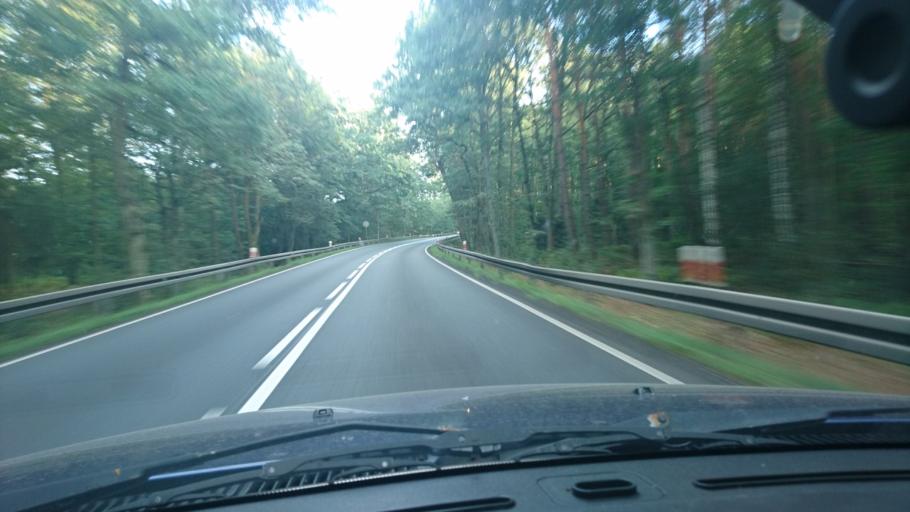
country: PL
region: Opole Voivodeship
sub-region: Powiat oleski
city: Olesno
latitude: 50.9374
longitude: 18.3295
